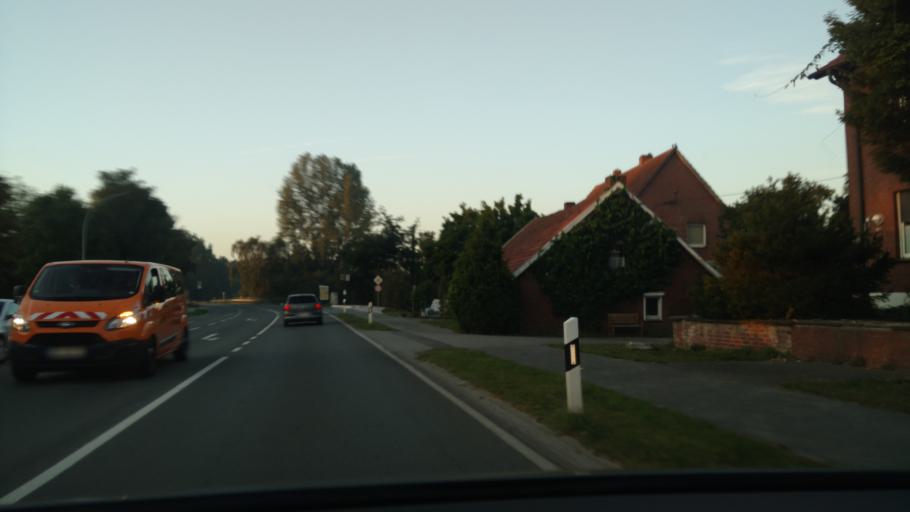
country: DE
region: North Rhine-Westphalia
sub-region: Regierungsbezirk Munster
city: Borken
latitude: 51.8581
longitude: 6.8415
